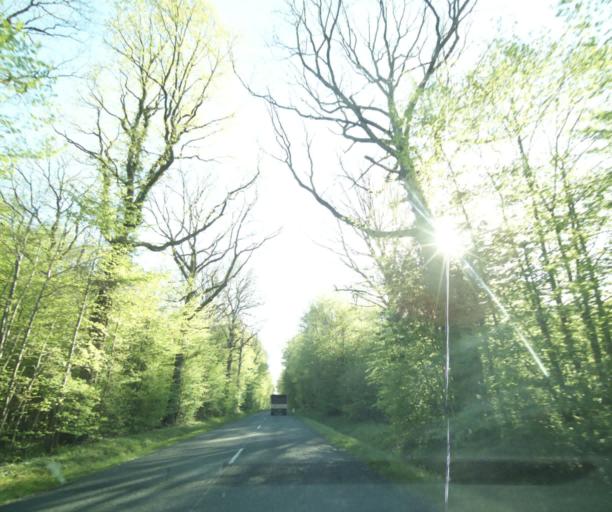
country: FR
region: Ile-de-France
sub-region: Departement de Seine-et-Marne
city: La Chapelle-Gauthier
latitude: 48.5094
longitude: 2.9259
